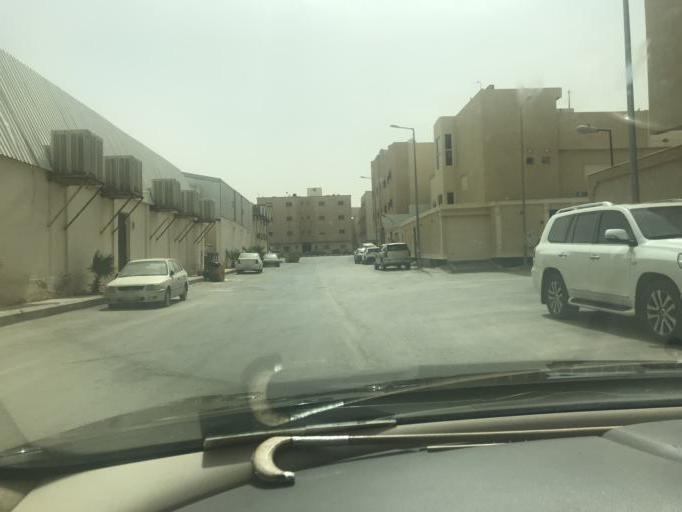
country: SA
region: Ar Riyad
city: Riyadh
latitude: 24.7909
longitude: 46.6906
